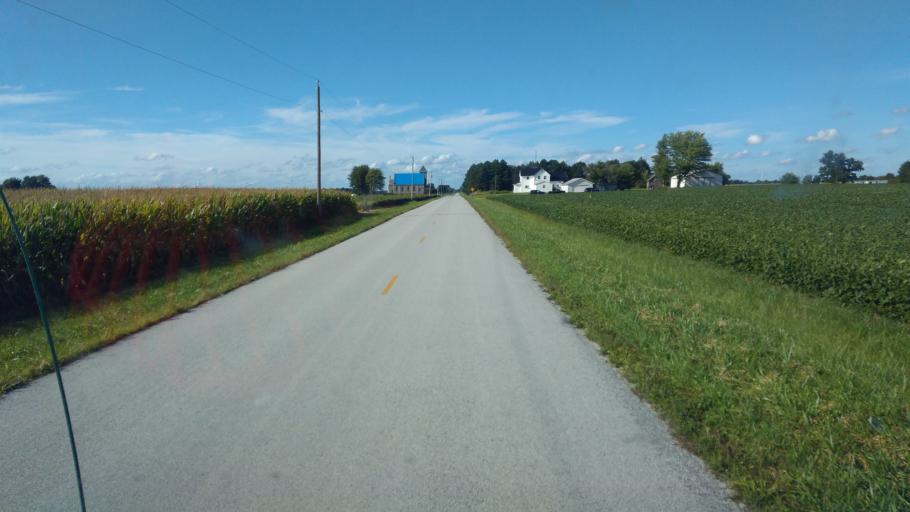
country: US
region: Ohio
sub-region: Hardin County
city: Kenton
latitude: 40.7427
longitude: -83.6907
